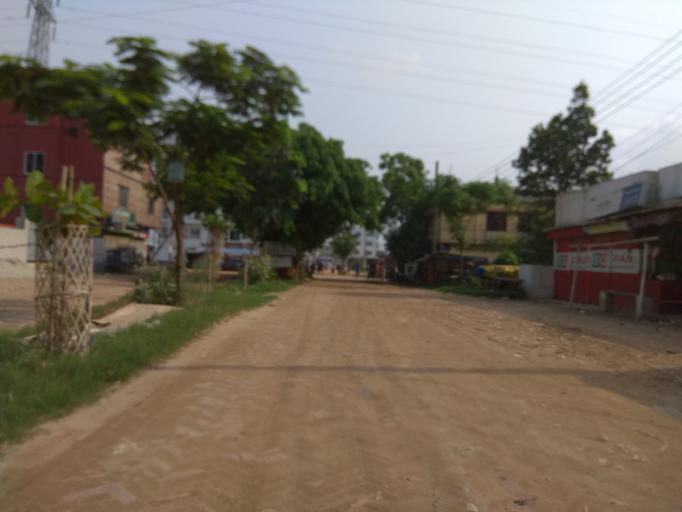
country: BD
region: Dhaka
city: Tungi
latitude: 23.8293
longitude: 90.3533
